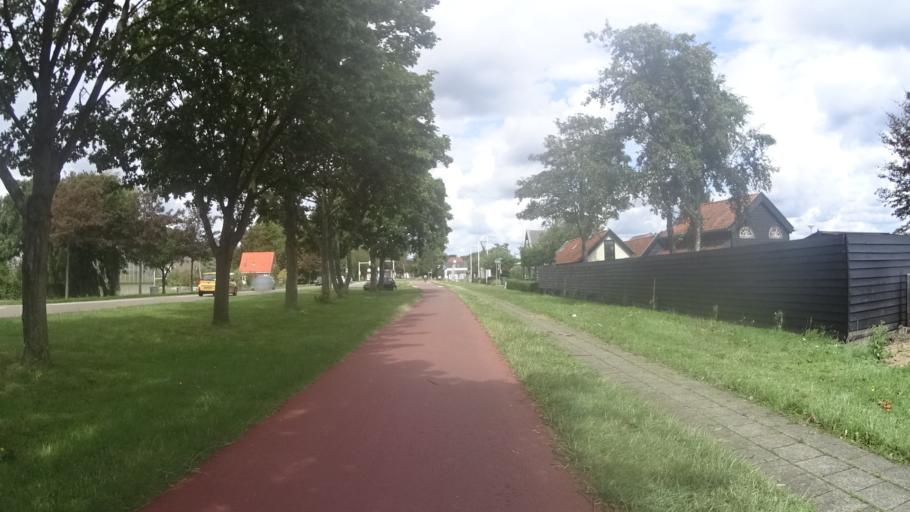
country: NL
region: North Holland
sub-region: Gemeente Heemskerk
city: Heemskerk
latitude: 52.5197
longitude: 4.6506
